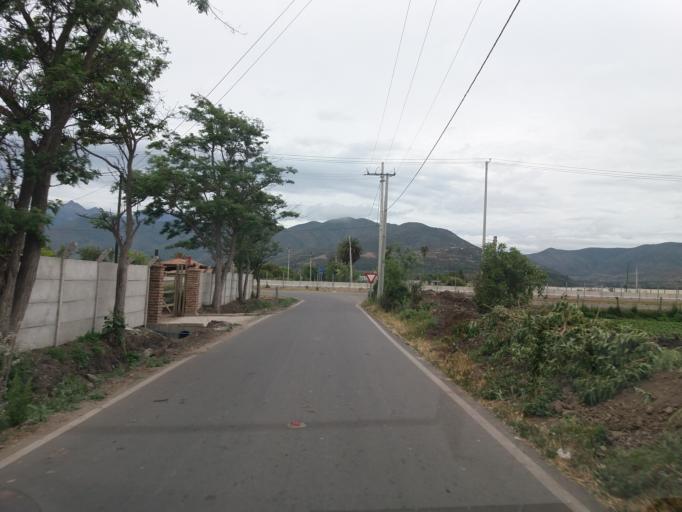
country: CL
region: Valparaiso
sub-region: Provincia de Quillota
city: Quillota
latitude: -32.9200
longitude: -71.2785
